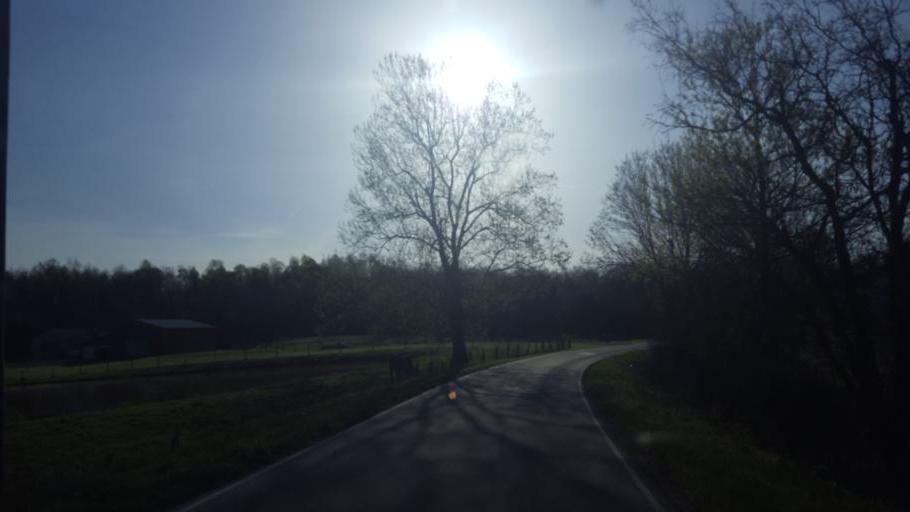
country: US
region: Kentucky
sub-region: Larue County
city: Hodgenville
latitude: 37.4844
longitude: -85.9287
